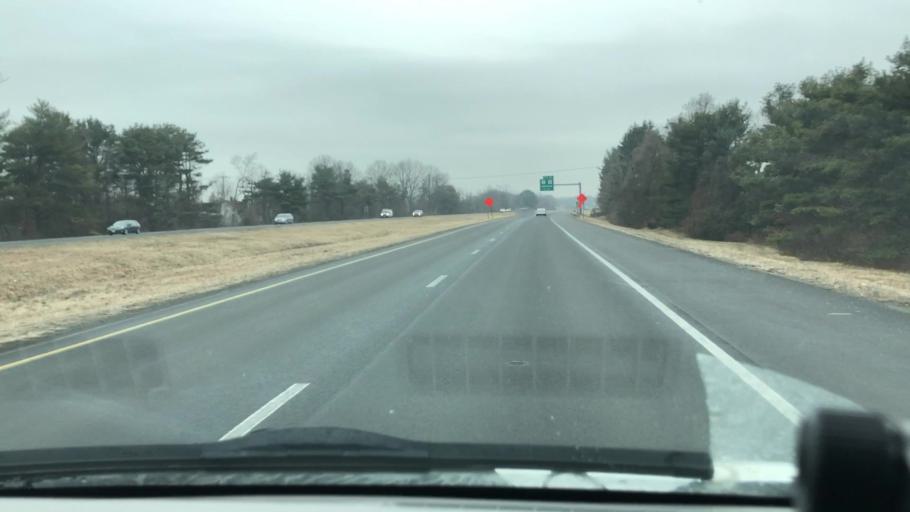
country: US
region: Massachusetts
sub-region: Hampshire County
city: Hatfield
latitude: 42.3720
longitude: -72.6334
